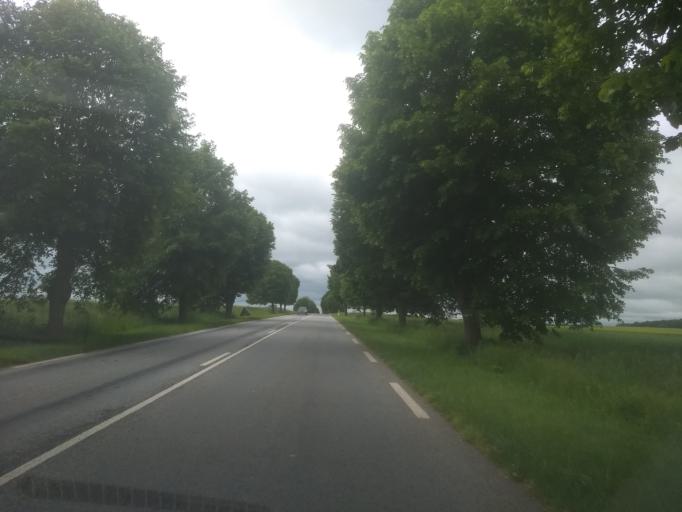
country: FR
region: Centre
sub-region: Departement d'Eure-et-Loir
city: Treon
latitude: 48.6603
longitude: 1.3049
